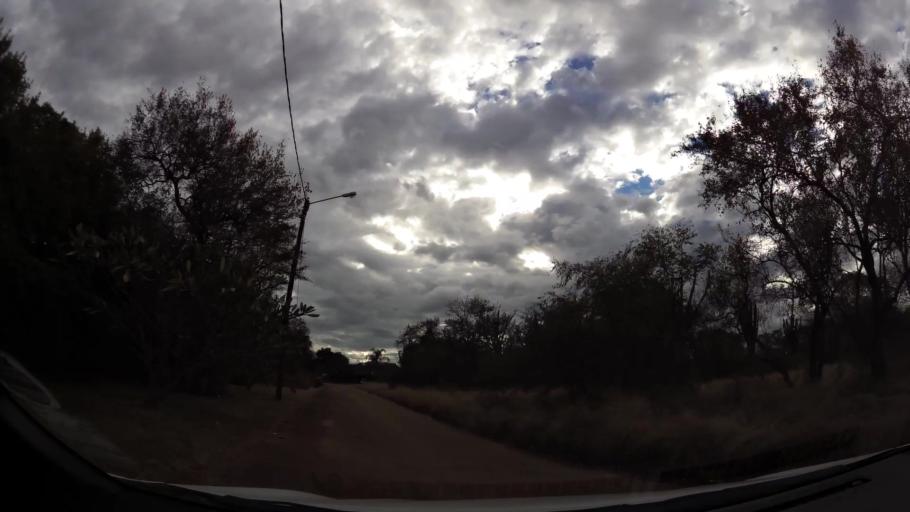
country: ZA
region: Limpopo
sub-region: Waterberg District Municipality
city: Modimolle
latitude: -24.5042
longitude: 28.7249
